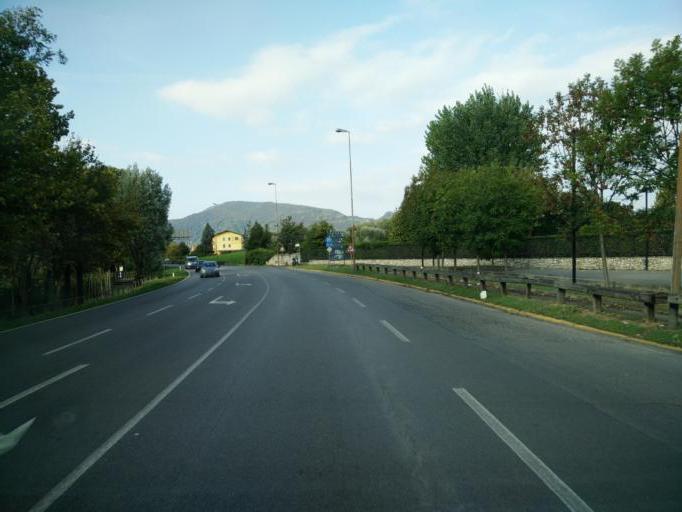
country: IT
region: Lombardy
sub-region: Provincia di Brescia
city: Iseo
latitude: 45.6552
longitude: 10.0353
